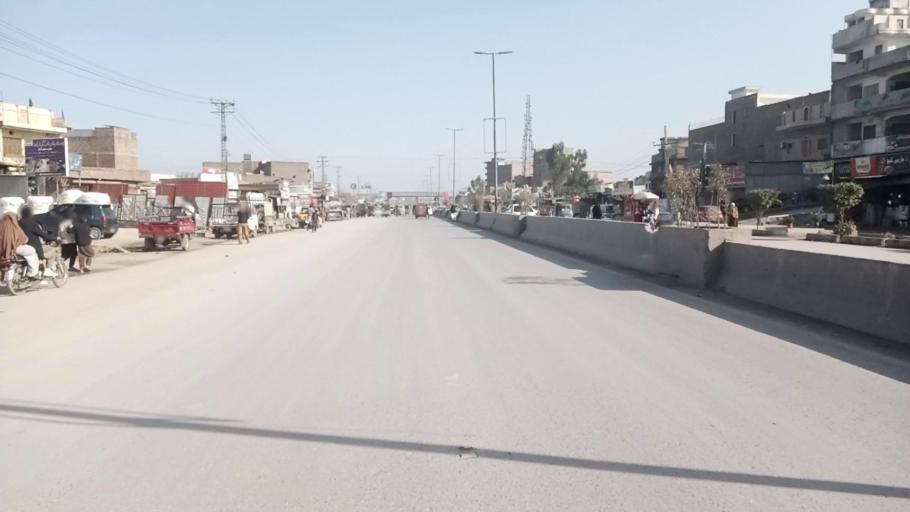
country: PK
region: Khyber Pakhtunkhwa
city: Peshawar
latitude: 34.0327
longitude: 71.5850
